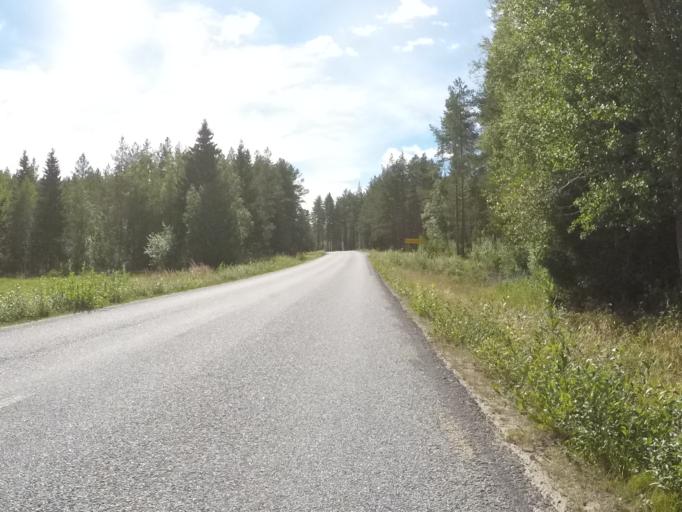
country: SE
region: Vaesterbotten
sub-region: Robertsfors Kommun
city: Robertsfors
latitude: 63.9649
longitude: 20.8104
